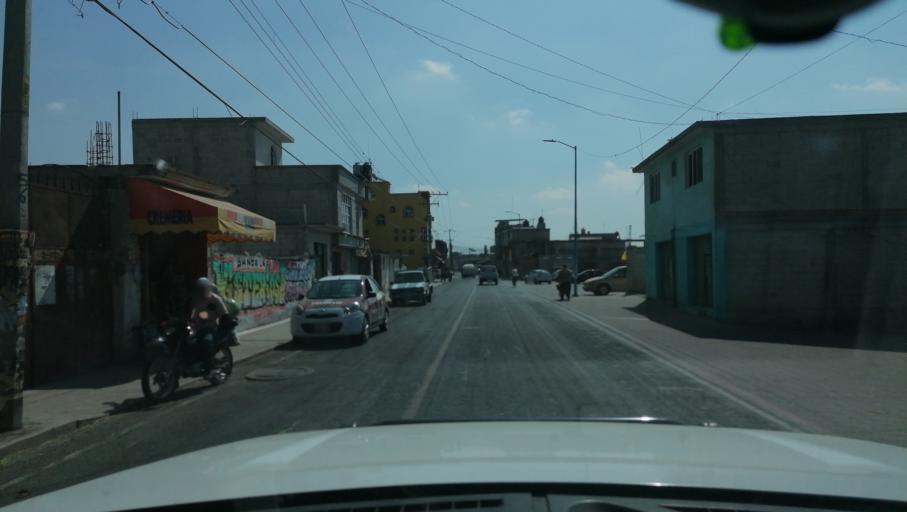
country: MX
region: Tlaxcala
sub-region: Tetlatlahuca
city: Tetlatlahuca
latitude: 19.2318
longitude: -98.2969
